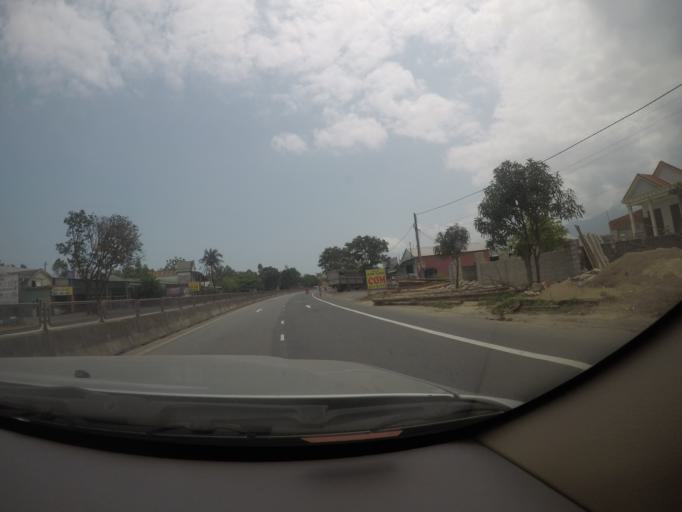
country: VN
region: Thua Thien-Hue
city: Phu Loc
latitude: 16.2633
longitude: 108.0558
